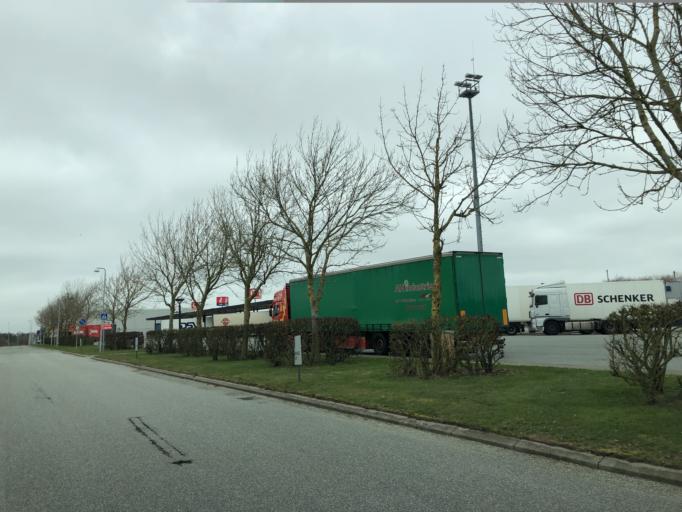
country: DK
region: North Denmark
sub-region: Frederikshavn Kommune
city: Saeby
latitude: 57.3122
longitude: 10.4503
